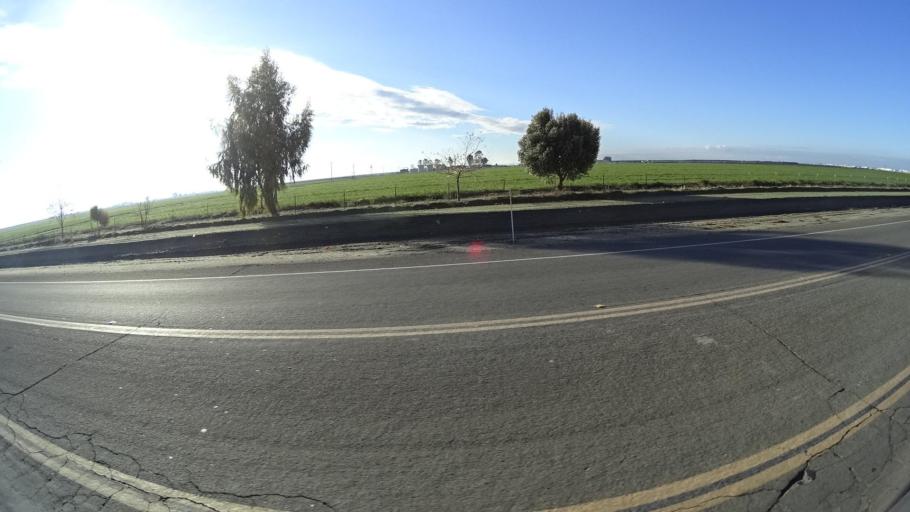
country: US
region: California
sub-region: Kern County
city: Delano
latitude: 35.7759
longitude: -119.3037
